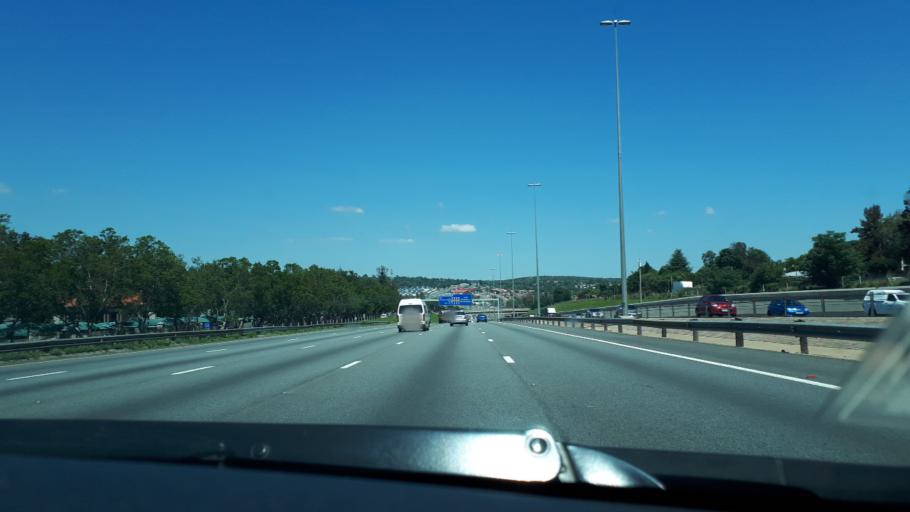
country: ZA
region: Gauteng
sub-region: City of Johannesburg Metropolitan Municipality
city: Midrand
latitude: -26.0407
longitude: 28.0747
